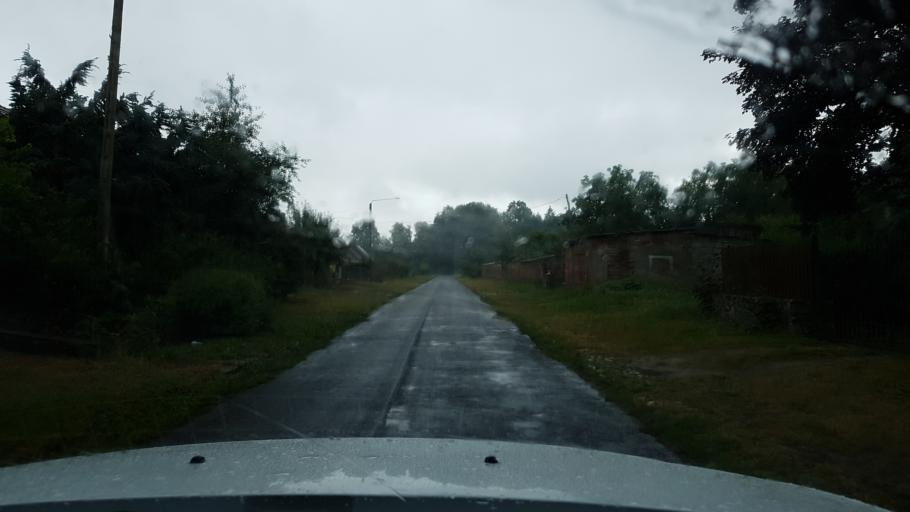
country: PL
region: West Pomeranian Voivodeship
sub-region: Powiat mysliborski
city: Barlinek
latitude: 52.9889
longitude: 15.1248
